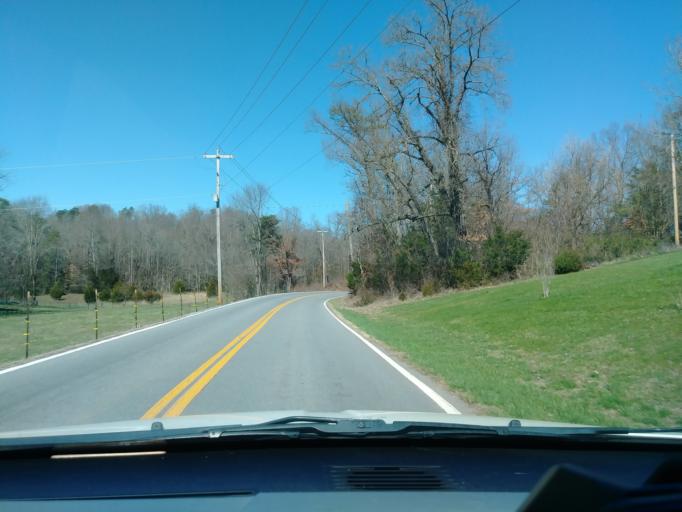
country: US
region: Tennessee
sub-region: Cocke County
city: Newport
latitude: 35.9778
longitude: -83.0604
